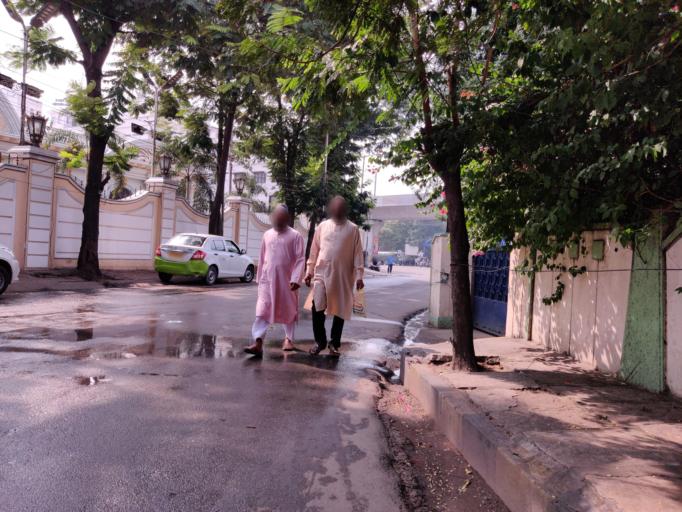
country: IN
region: Telangana
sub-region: Hyderabad
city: Hyderabad
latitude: 17.3961
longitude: 78.4720
